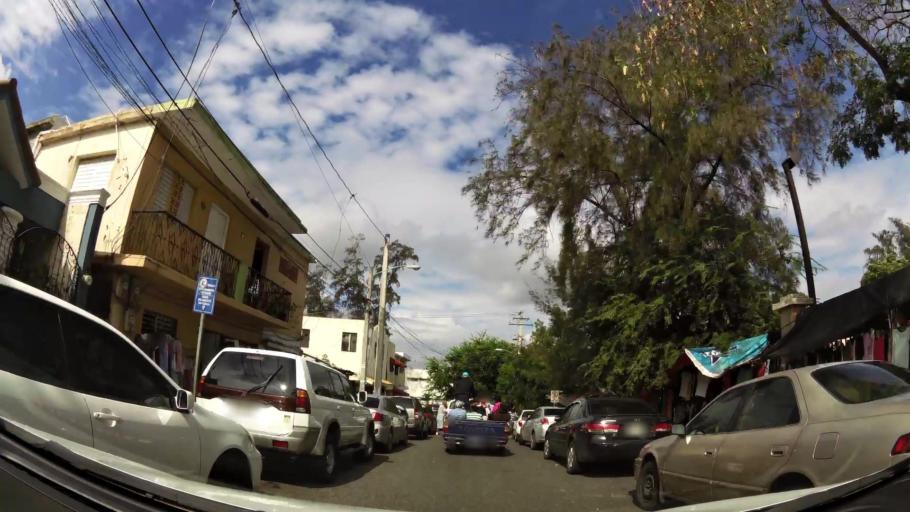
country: DO
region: Santiago
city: Santiago de los Caballeros
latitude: 19.4553
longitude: -70.6985
